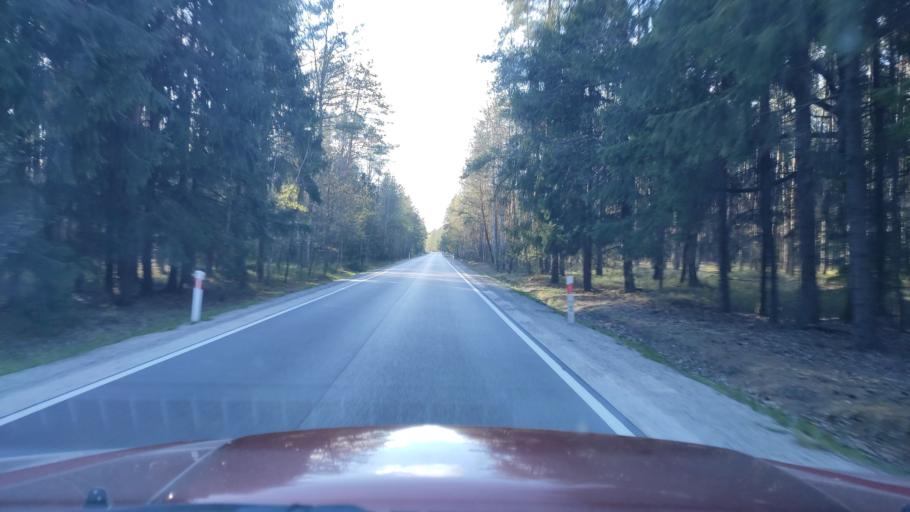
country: PL
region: Masovian Voivodeship
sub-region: Powiat zwolenski
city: Zwolen
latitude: 51.4045
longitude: 21.5319
